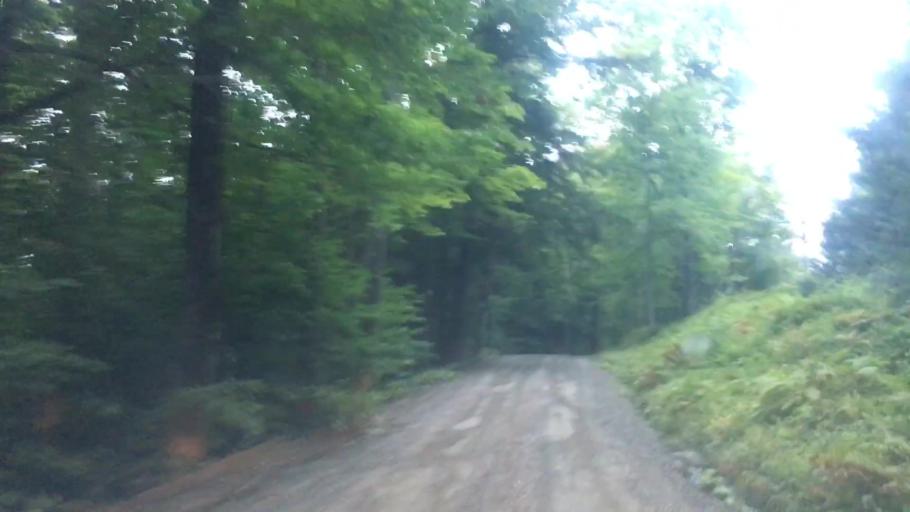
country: US
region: Vermont
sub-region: Windham County
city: Dover
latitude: 42.8368
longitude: -72.7677
